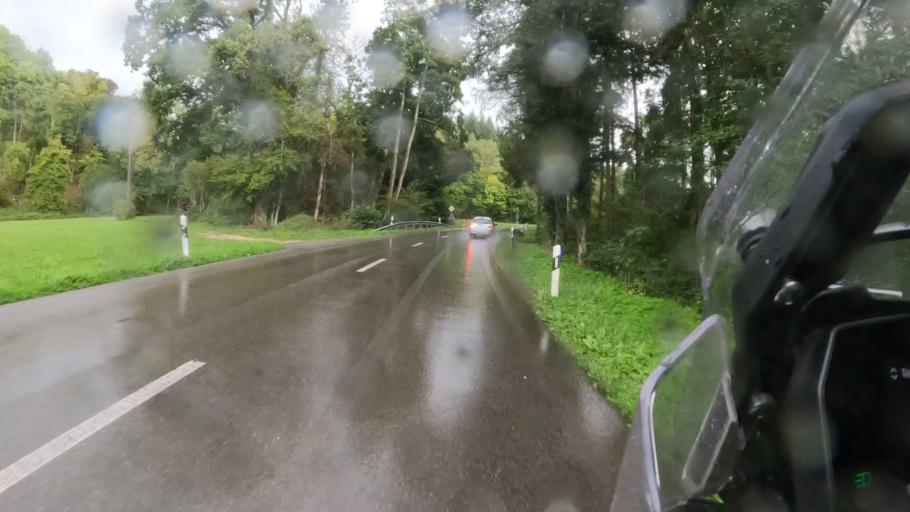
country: DE
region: Baden-Wuerttemberg
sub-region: Freiburg Region
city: Jestetten
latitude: 47.6459
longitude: 8.5300
